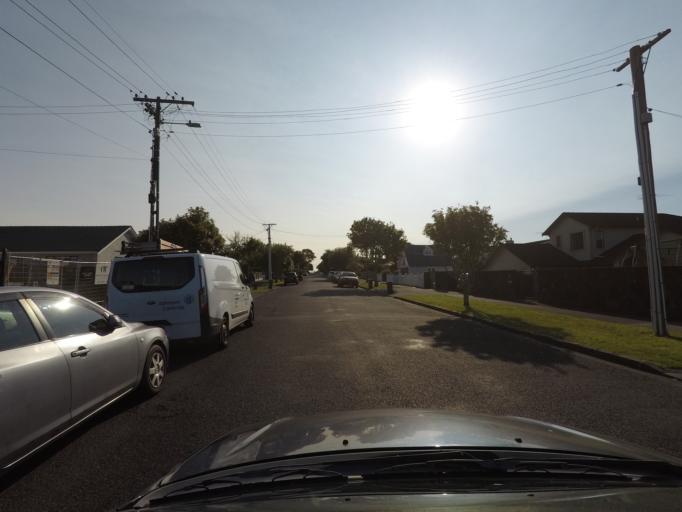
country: NZ
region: Auckland
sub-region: Auckland
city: Rosebank
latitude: -36.8615
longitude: 174.7070
